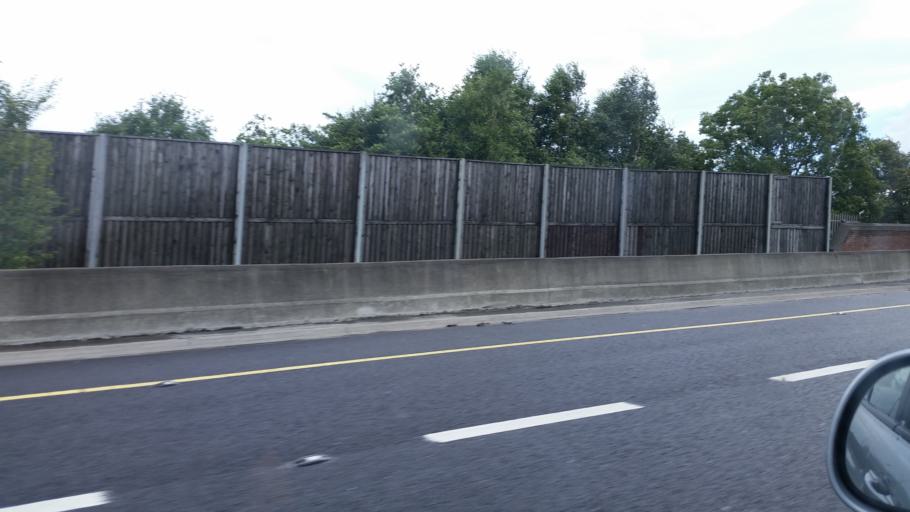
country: IE
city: Cherry Orchard
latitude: 53.3341
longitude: -6.3836
